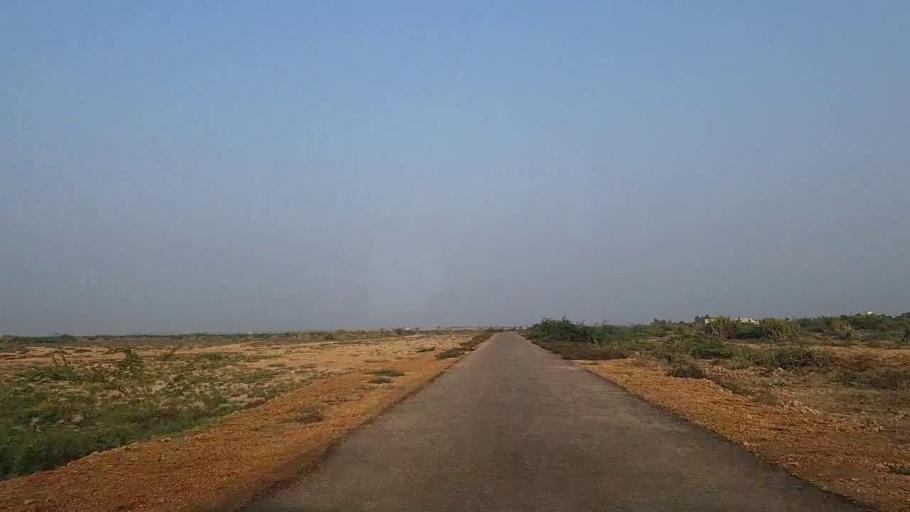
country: PK
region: Sindh
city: Thatta
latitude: 24.6904
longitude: 67.8400
